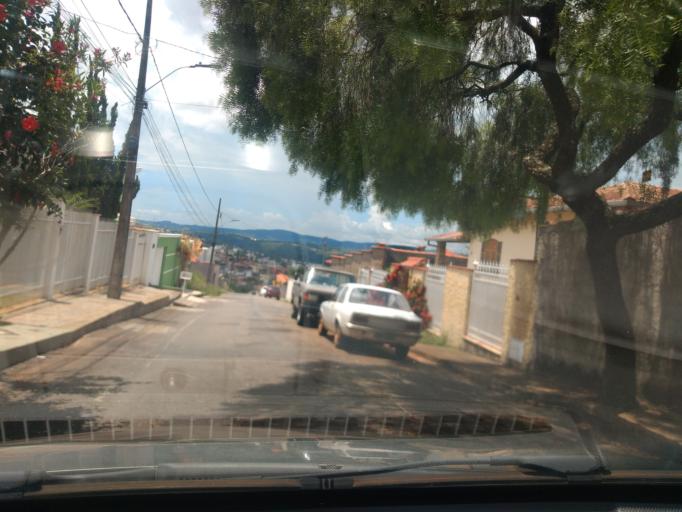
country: BR
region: Minas Gerais
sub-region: Tres Coracoes
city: Tres Coracoes
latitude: -21.6894
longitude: -45.2643
